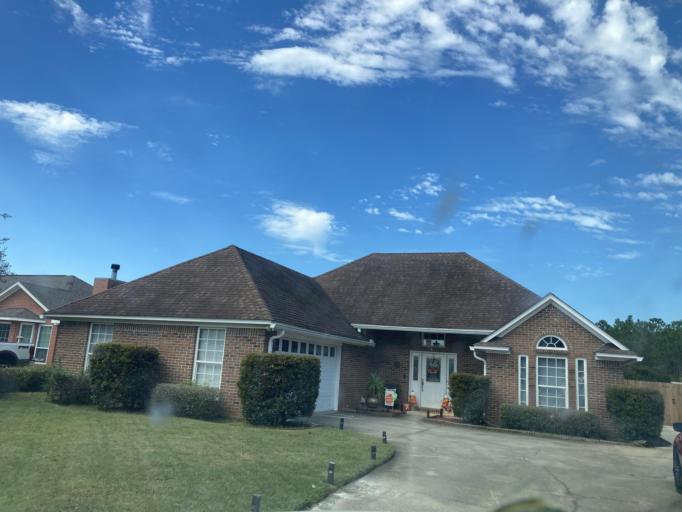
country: US
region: Mississippi
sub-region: Jackson County
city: Saint Martin
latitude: 30.4387
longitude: -88.8561
